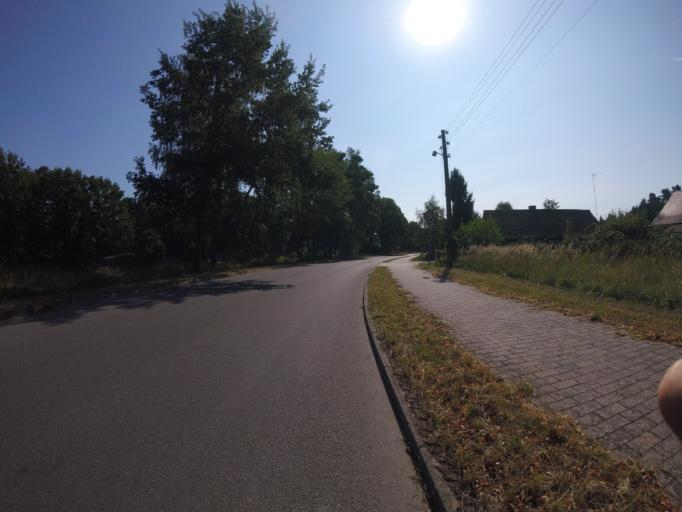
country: DE
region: Brandenburg
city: Mullrose
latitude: 52.2643
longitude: 14.3673
